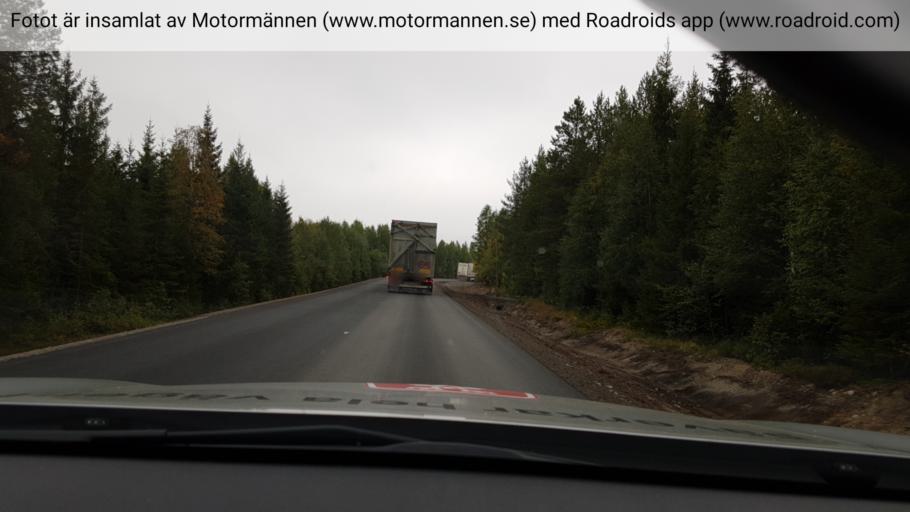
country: SE
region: Vaesterbotten
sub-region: Skelleftea Kommun
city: Burtraesk
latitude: 64.3977
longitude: 20.5489
